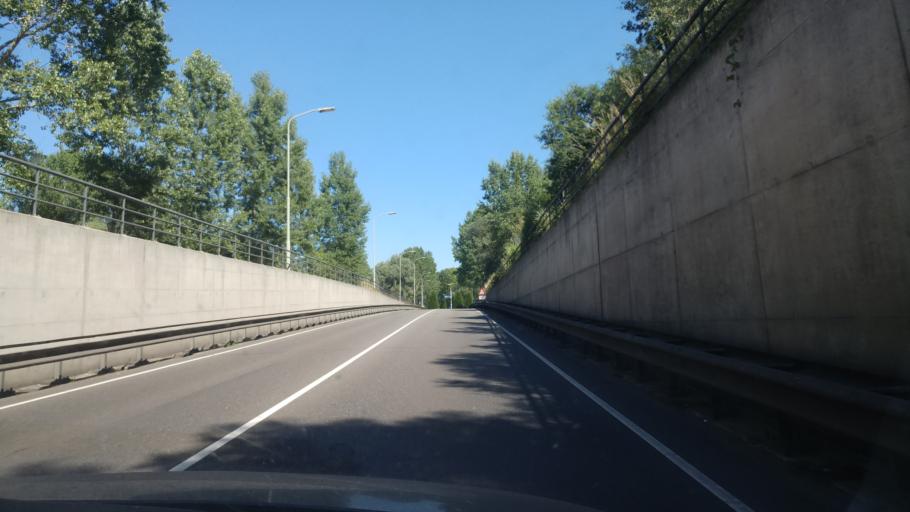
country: NL
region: North Brabant
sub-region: Gemeente Boxtel
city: Boxtel
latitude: 51.5745
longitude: 5.3309
